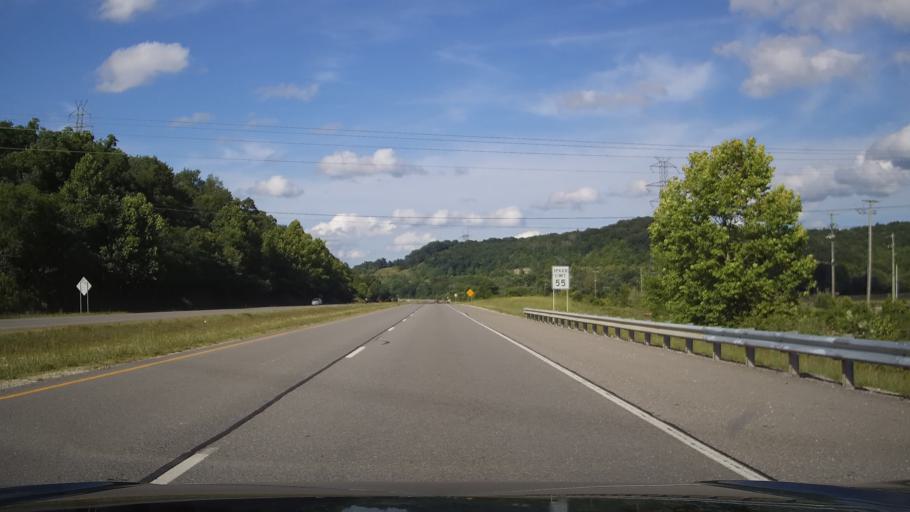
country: US
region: Kentucky
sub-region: Lawrence County
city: Louisa
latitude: 38.1741
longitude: -82.6188
